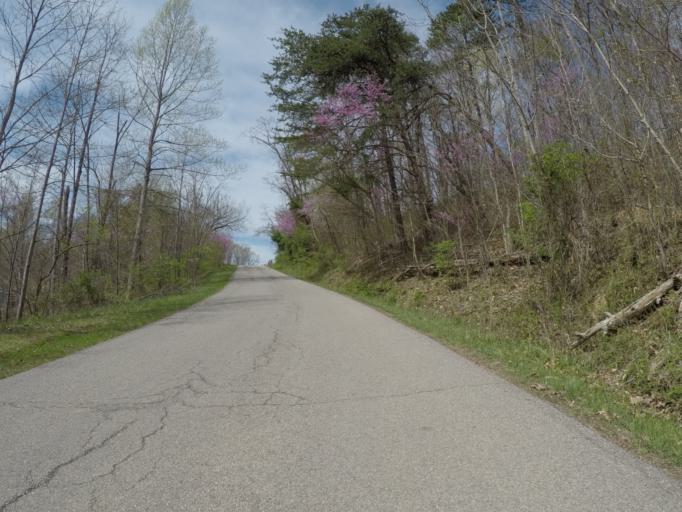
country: US
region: West Virginia
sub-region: Wayne County
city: Lavalette
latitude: 38.3545
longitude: -82.4043
